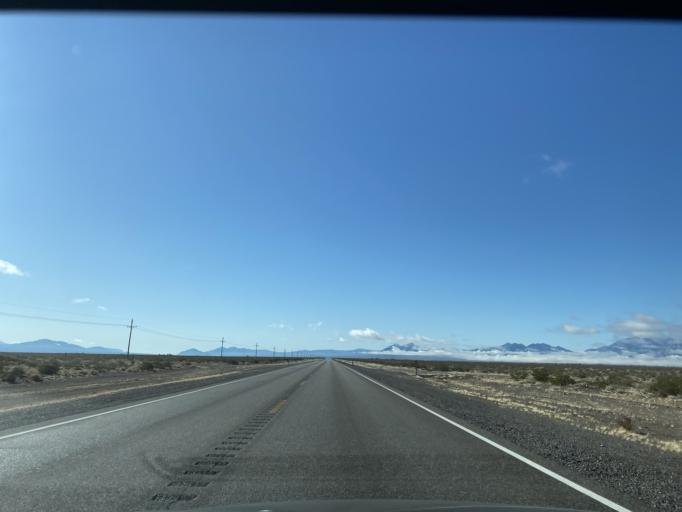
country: US
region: Nevada
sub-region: Nye County
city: Beatty
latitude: 36.6011
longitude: -116.4079
